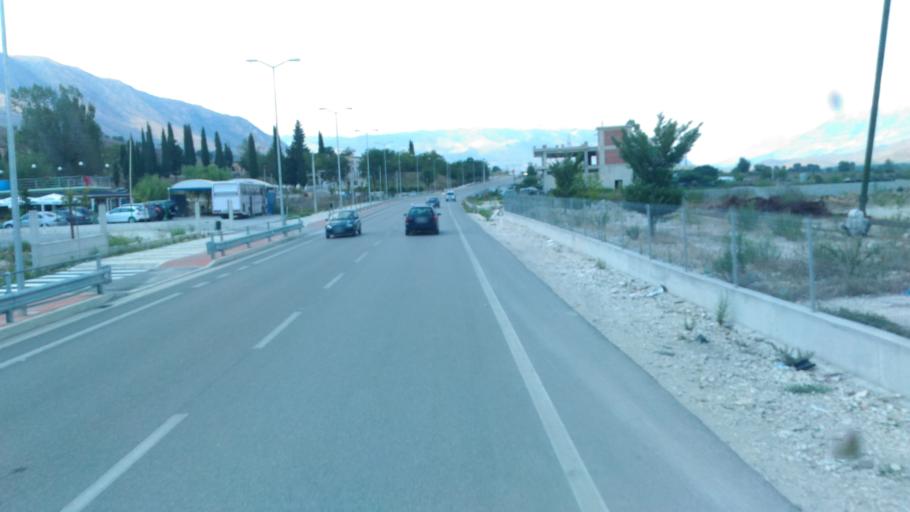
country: AL
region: Gjirokaster
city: Gjirokaster
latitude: 40.0895
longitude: 20.1388
